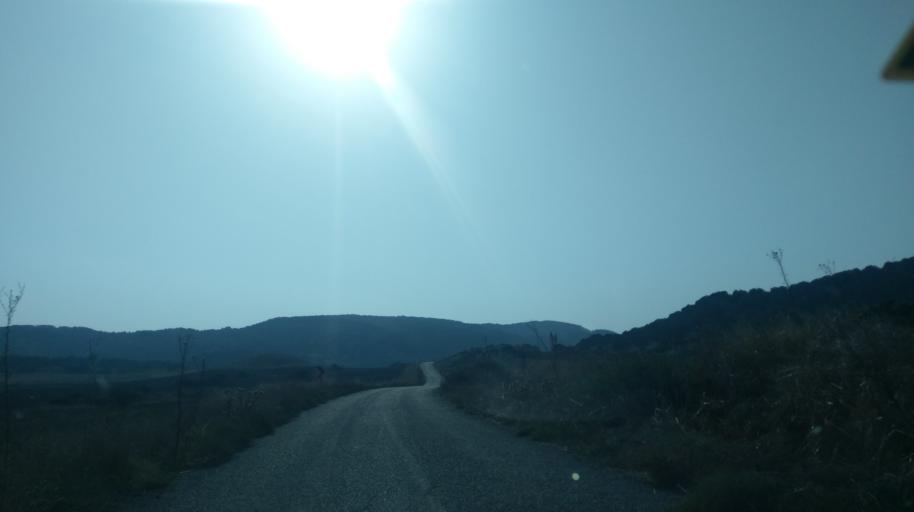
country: CY
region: Ammochostos
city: Rizokarpaso
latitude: 35.5581
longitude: 34.3726
